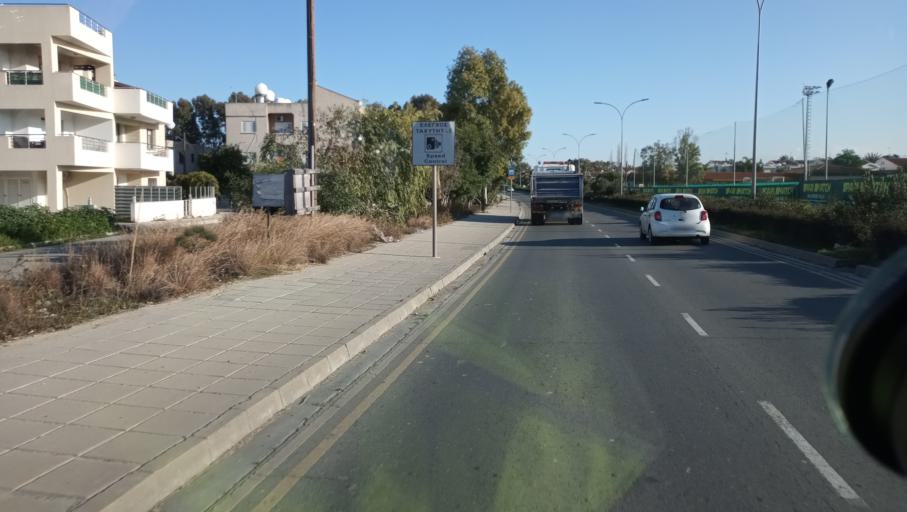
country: CY
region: Lefkosia
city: Kato Deftera
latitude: 35.1340
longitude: 33.3119
